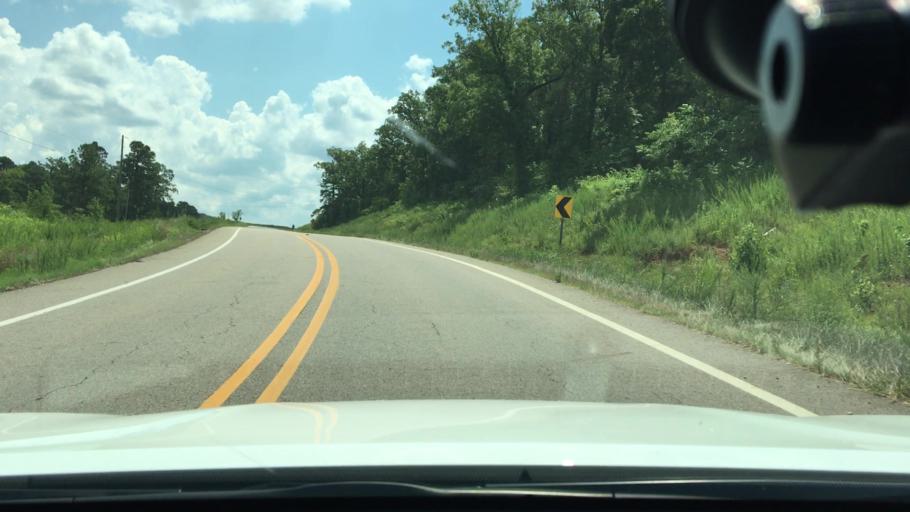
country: US
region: Arkansas
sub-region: Logan County
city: Paris
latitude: 35.2563
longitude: -93.6815
